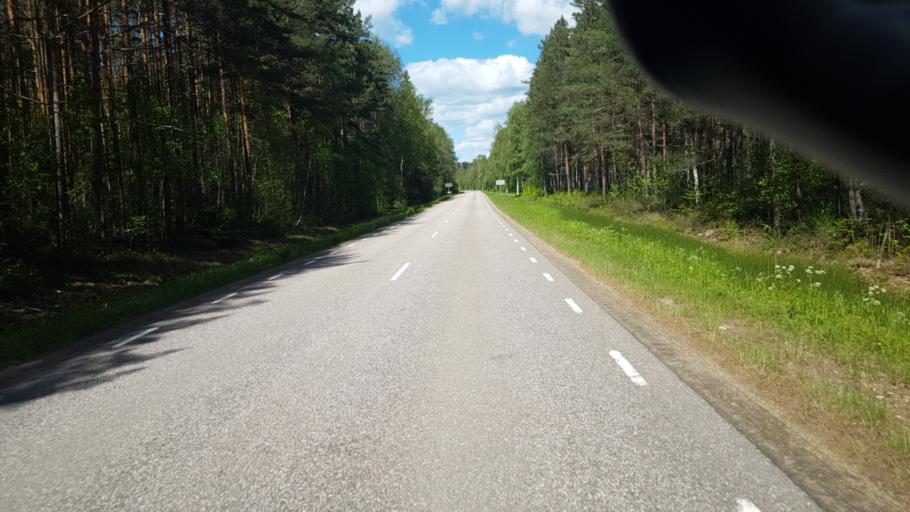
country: SE
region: Vaermland
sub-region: Arvika Kommun
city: Arvika
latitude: 59.6564
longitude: 12.8882
